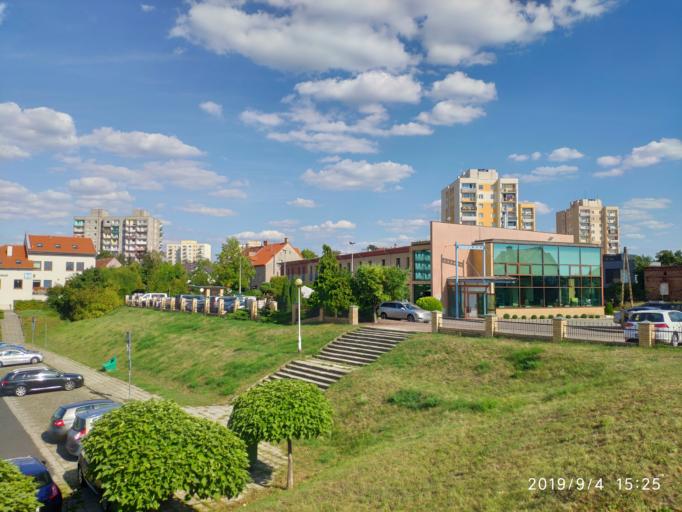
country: PL
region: Lubusz
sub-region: Zielona Gora
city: Zielona Gora
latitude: 51.9382
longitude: 15.5147
